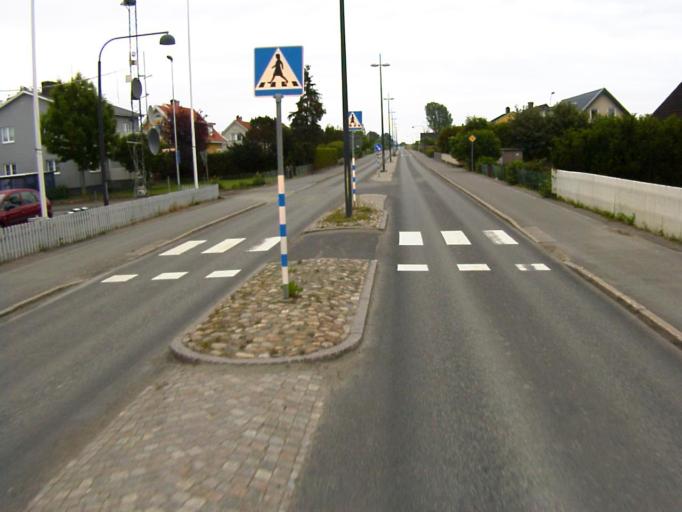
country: SE
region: Skane
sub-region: Kristianstads Kommun
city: Kristianstad
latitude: 56.0289
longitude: 14.1936
